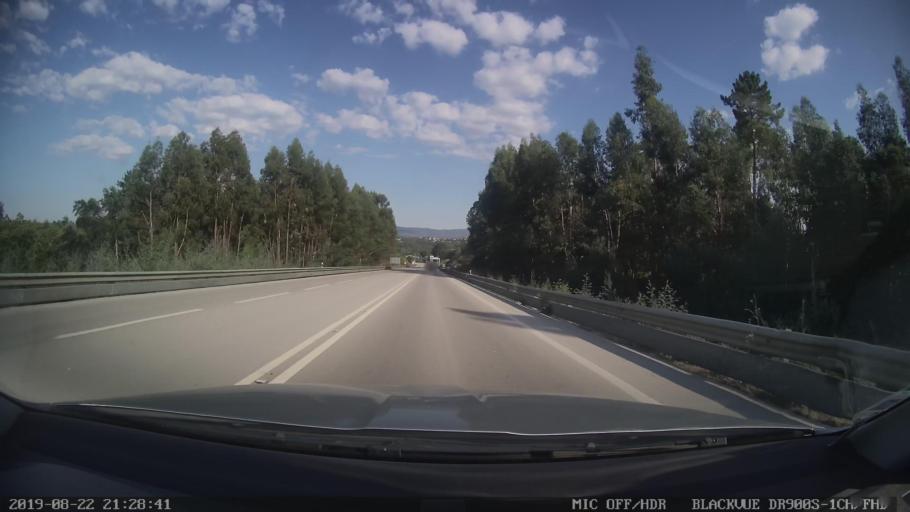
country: PT
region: Leiria
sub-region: Pedrogao Grande
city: Pedrogao Grande
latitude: 39.8957
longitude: -8.1234
